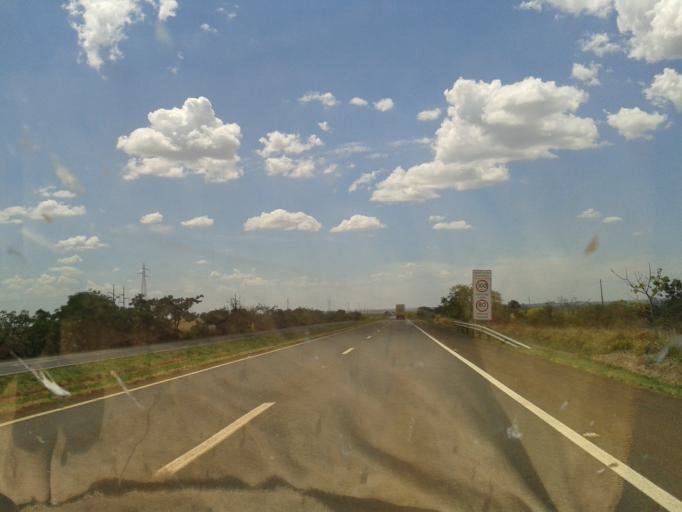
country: BR
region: Minas Gerais
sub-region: Uberlandia
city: Uberlandia
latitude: -19.0681
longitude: -48.1910
